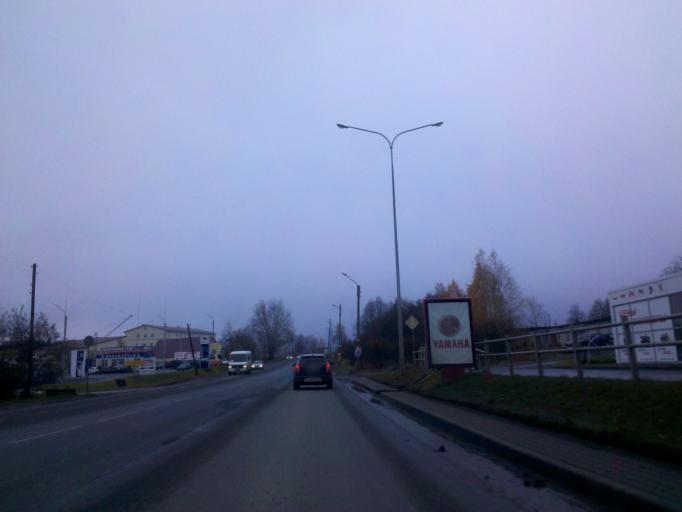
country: RU
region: Republic of Karelia
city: Petrozavodsk
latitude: 61.8174
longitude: 34.2802
